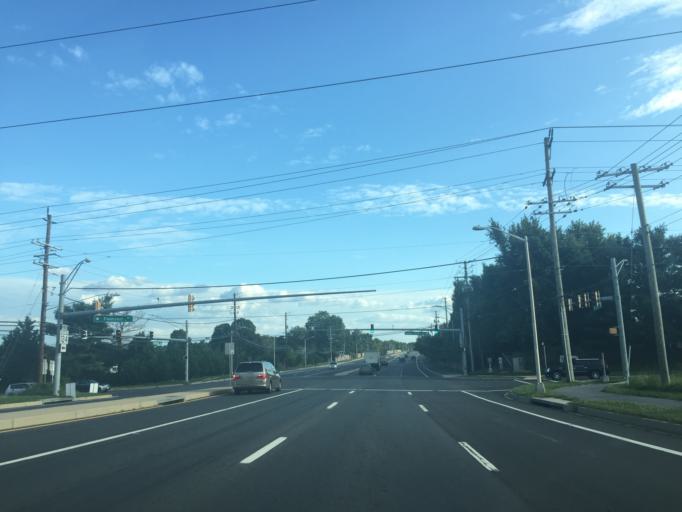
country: US
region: Maryland
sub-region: Montgomery County
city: Redland
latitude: 39.1859
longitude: -77.1509
